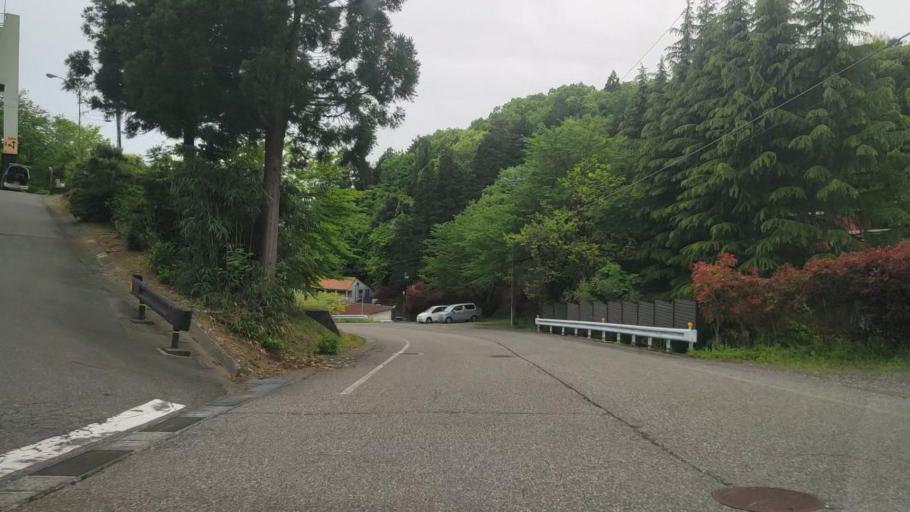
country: JP
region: Niigata
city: Kamo
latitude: 37.7156
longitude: 139.0827
